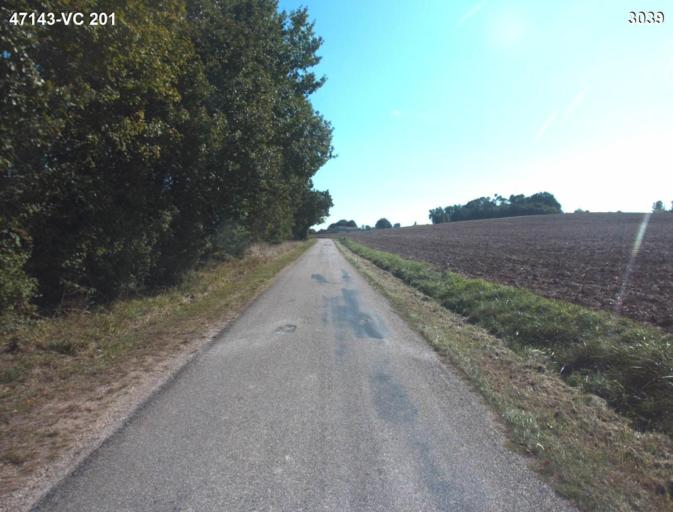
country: FR
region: Aquitaine
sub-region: Departement du Lot-et-Garonne
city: Vianne
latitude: 44.1795
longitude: 0.3408
